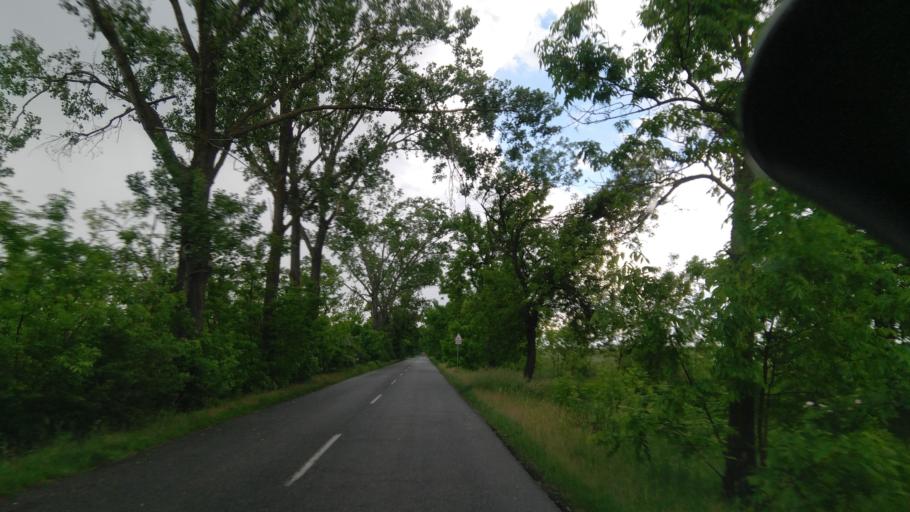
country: HU
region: Bekes
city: Fuzesgyarmat
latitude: 47.1355
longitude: 21.1584
